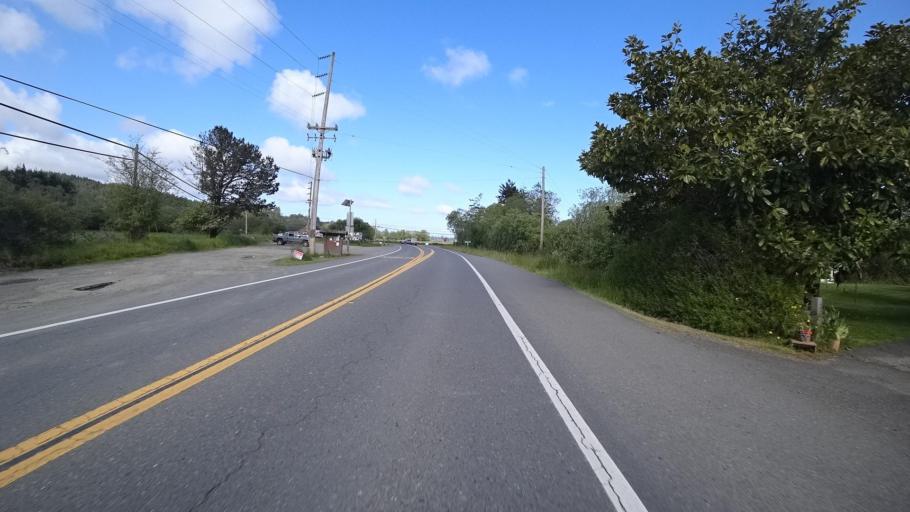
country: US
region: California
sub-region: Humboldt County
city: Myrtletown
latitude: 40.7852
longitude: -124.0839
